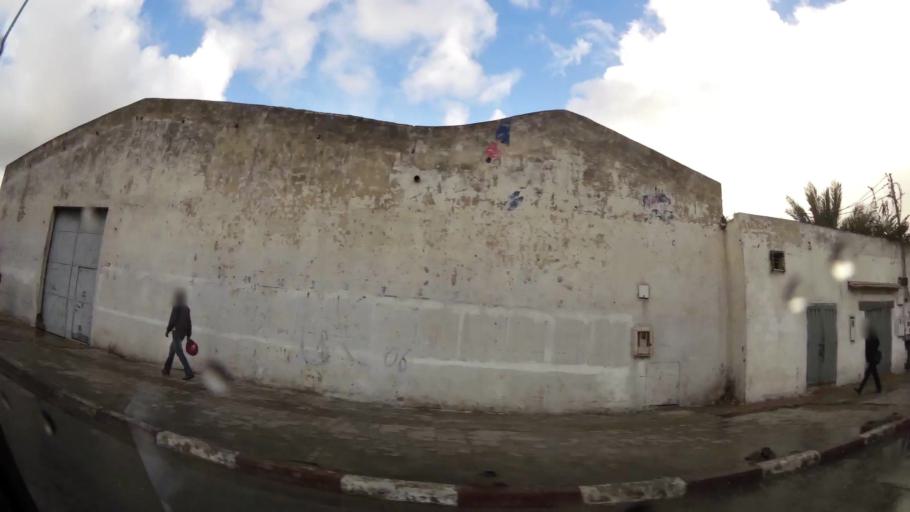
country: MA
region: Grand Casablanca
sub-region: Casablanca
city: Casablanca
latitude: 33.5565
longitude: -7.5936
